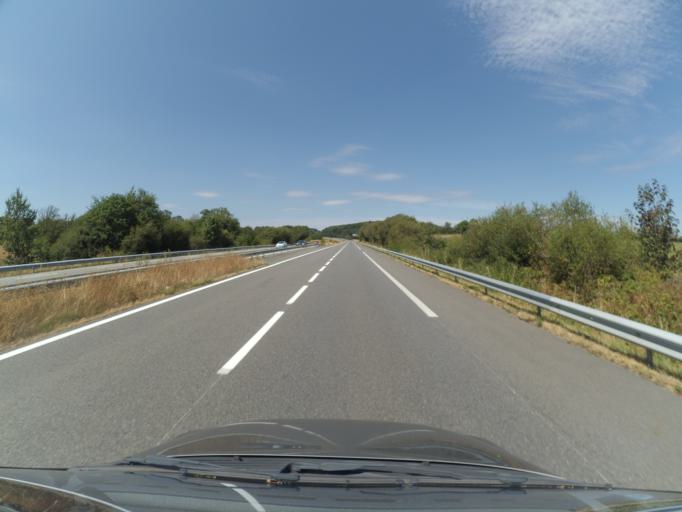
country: FR
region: Limousin
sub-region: Departement de la Creuse
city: La Souterraine
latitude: 46.2241
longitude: 1.4826
